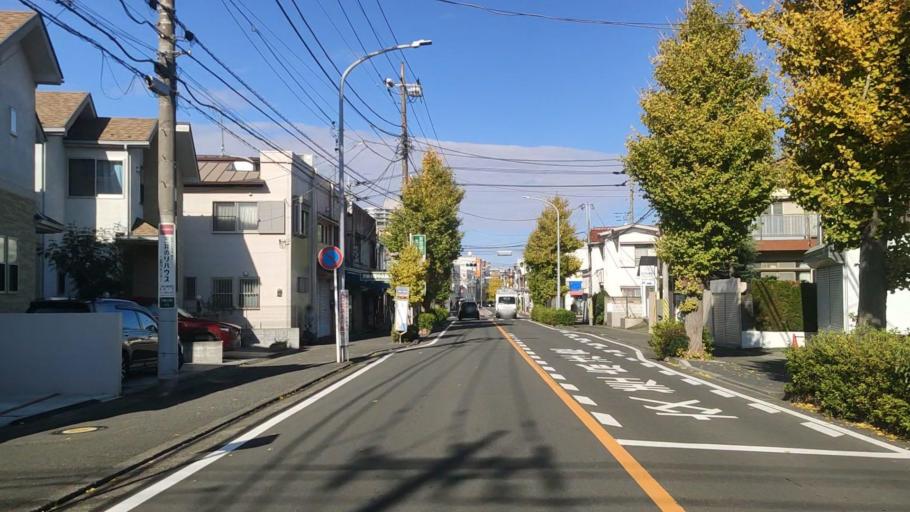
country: JP
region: Kanagawa
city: Minami-rinkan
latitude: 35.4566
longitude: 139.5343
